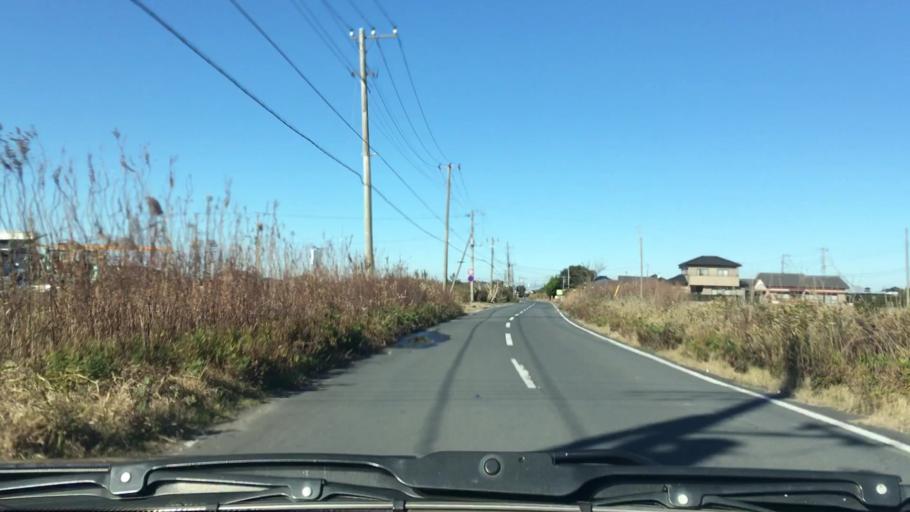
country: JP
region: Chiba
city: Omigawa
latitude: 35.8741
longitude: 140.6345
